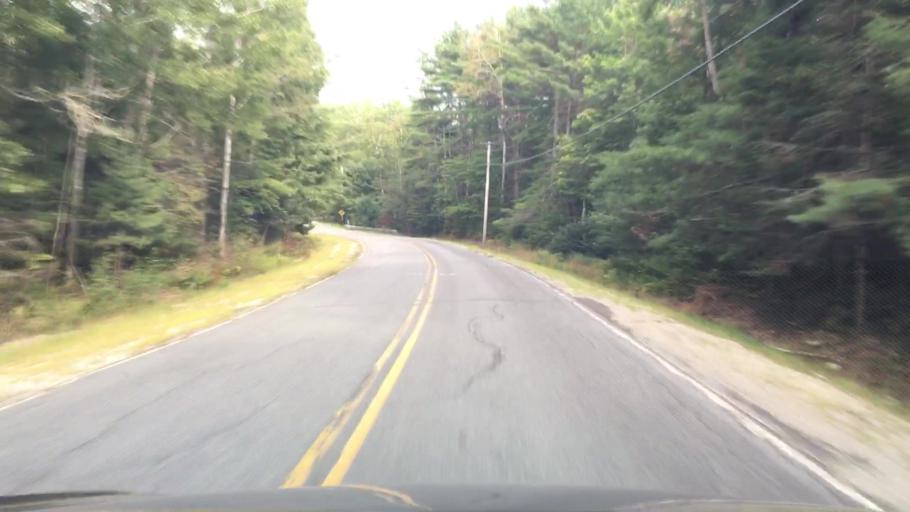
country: US
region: Maine
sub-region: Hancock County
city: Surry
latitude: 44.4978
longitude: -68.5420
